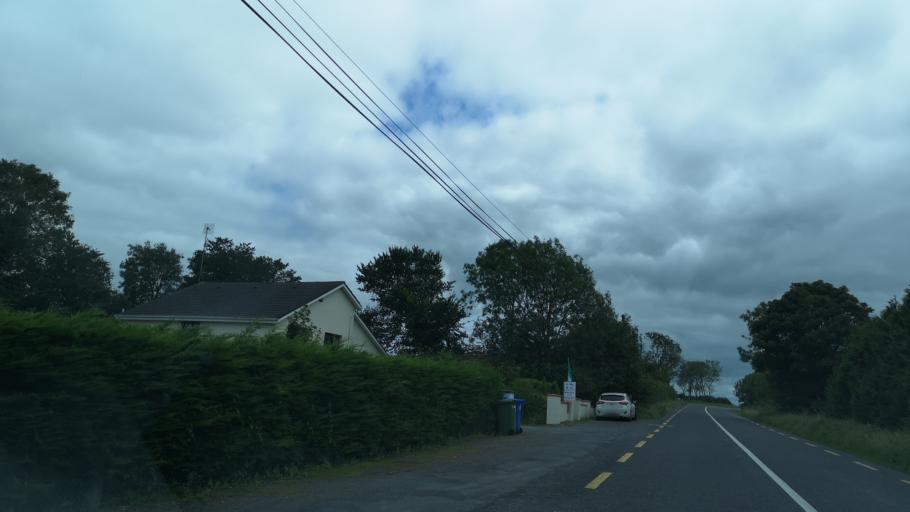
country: IE
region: Connaught
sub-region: County Galway
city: Ballinasloe
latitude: 53.3187
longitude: -8.1752
